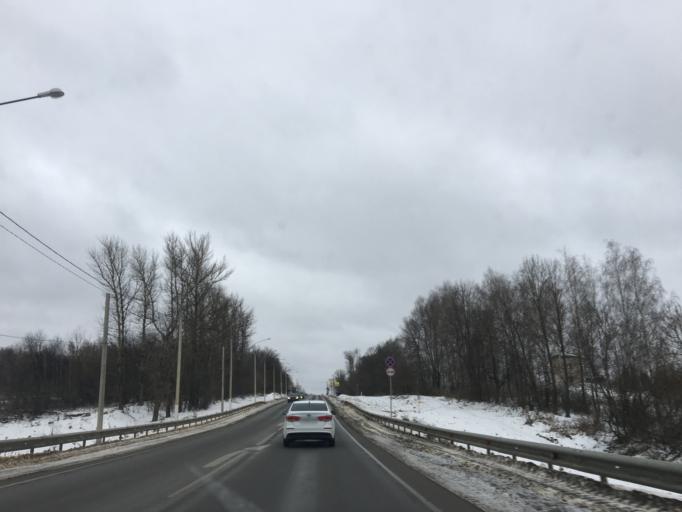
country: RU
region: Tula
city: Pervomayskiy
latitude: 54.0742
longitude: 37.5408
